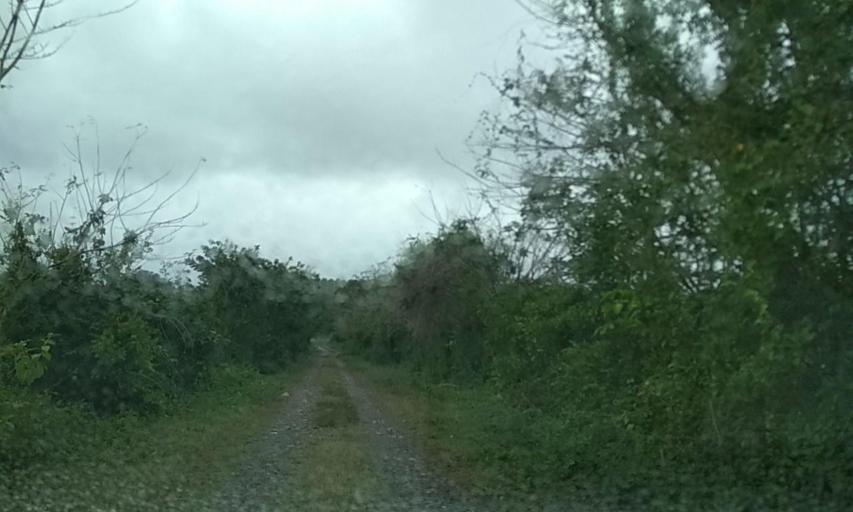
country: MX
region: Veracruz
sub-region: Papantla
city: El Chote
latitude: 20.3767
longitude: -97.3447
